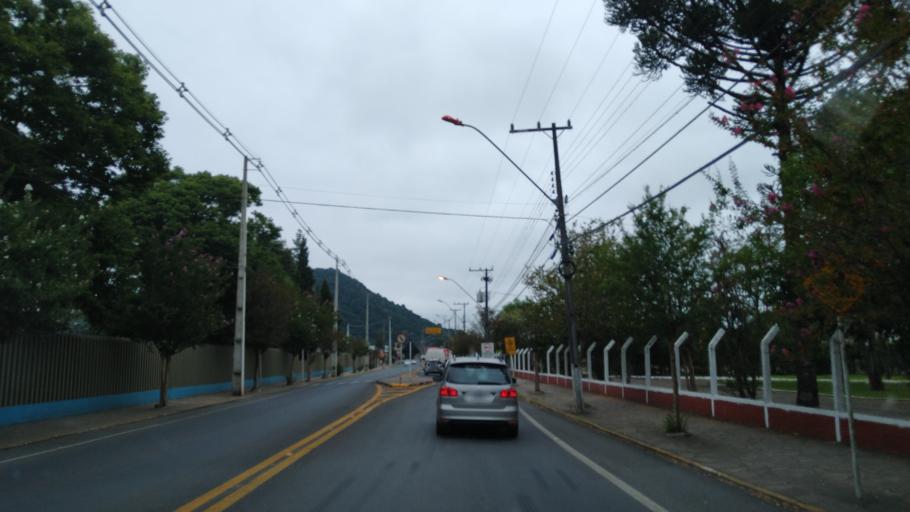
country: BR
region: Santa Catarina
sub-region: Porto Uniao
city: Porto Uniao
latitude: -26.2577
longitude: -51.0669
